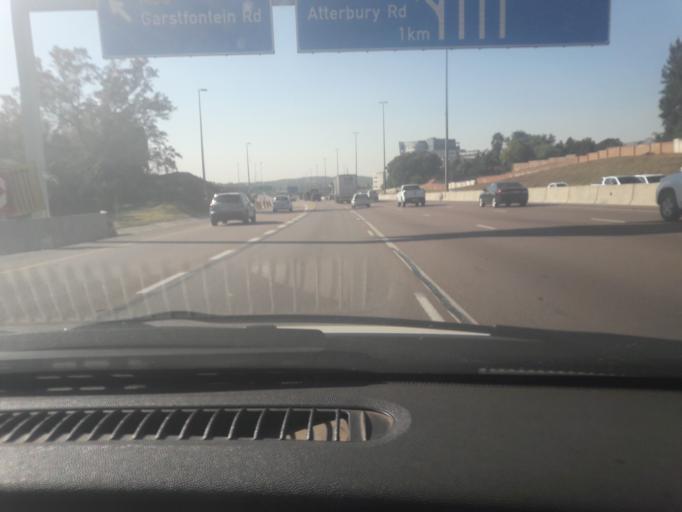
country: ZA
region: Gauteng
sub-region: City of Tshwane Metropolitan Municipality
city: Pretoria
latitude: -25.7902
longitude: 28.2686
